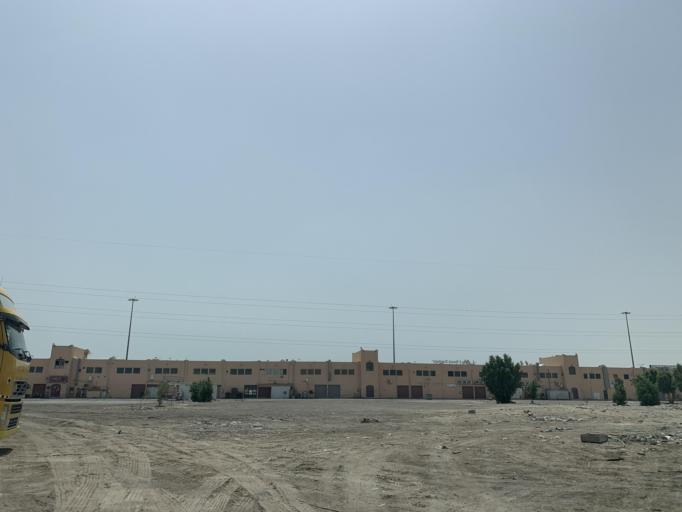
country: BH
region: Northern
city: Sitrah
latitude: 26.1286
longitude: 50.5953
